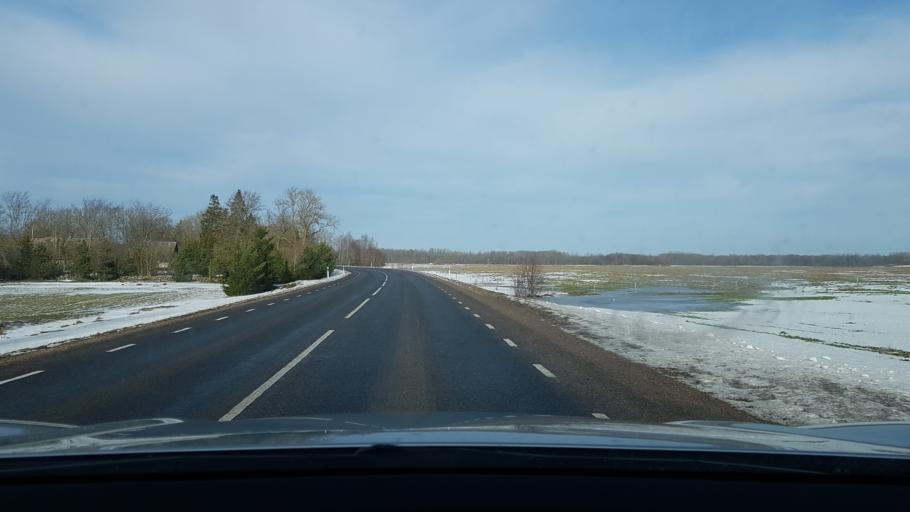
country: EE
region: Saare
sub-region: Kuressaare linn
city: Kuressaare
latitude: 58.2937
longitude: 22.5417
